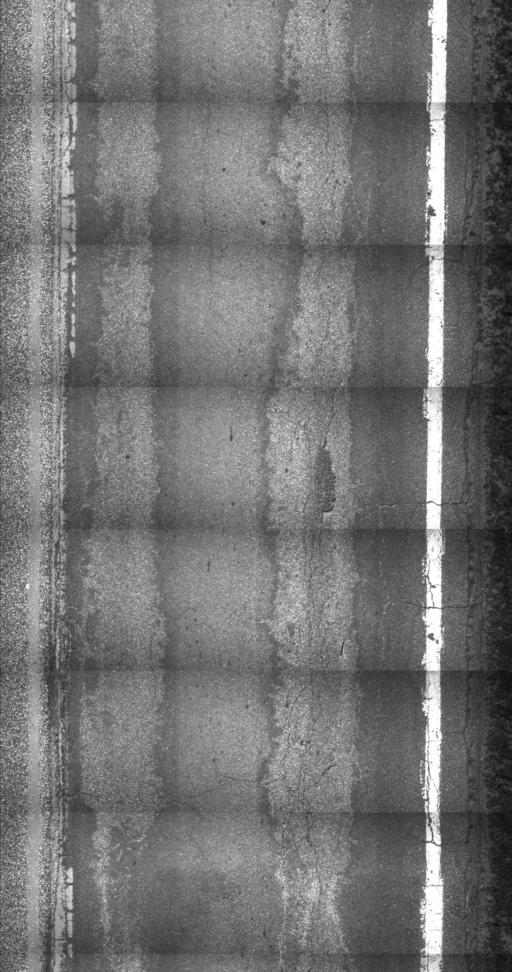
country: US
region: Vermont
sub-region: Orange County
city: Williamstown
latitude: 44.0208
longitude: -72.5707
